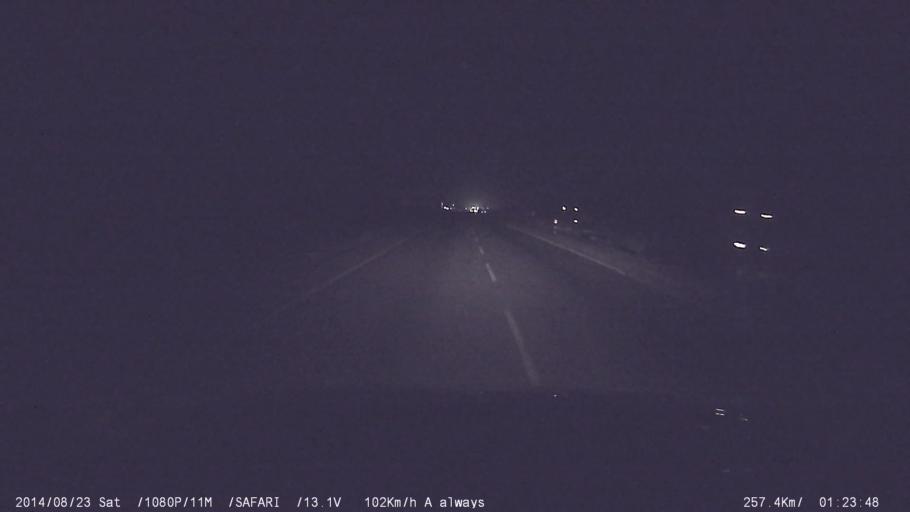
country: IN
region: Tamil Nadu
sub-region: Kancheepuram
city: Kanchipuram
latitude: 12.8709
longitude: 79.6418
